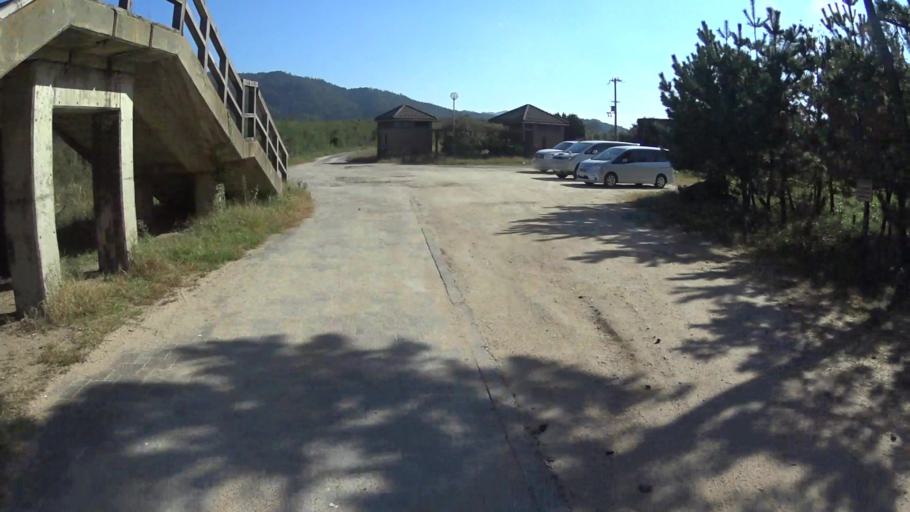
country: JP
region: Kyoto
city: Miyazu
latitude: 35.7434
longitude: 135.1063
